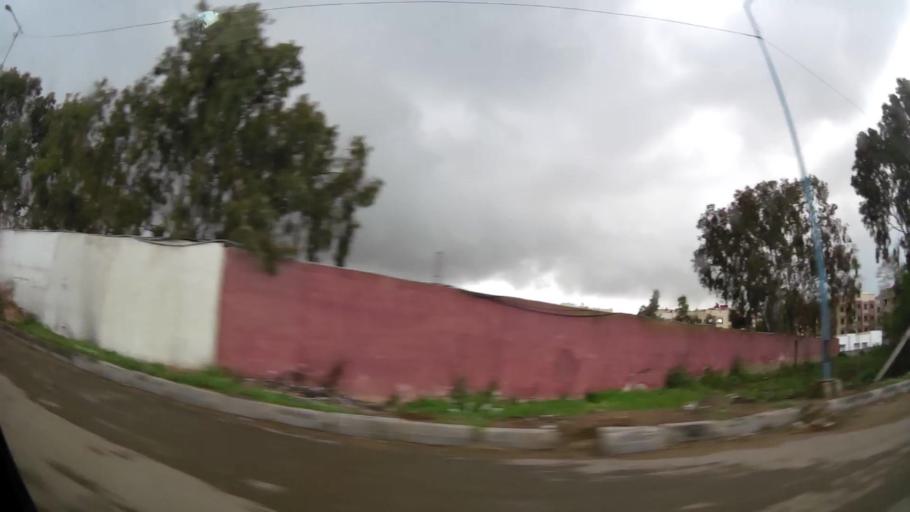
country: MA
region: Grand Casablanca
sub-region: Mediouna
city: Tit Mellil
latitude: 33.5671
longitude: -7.5080
